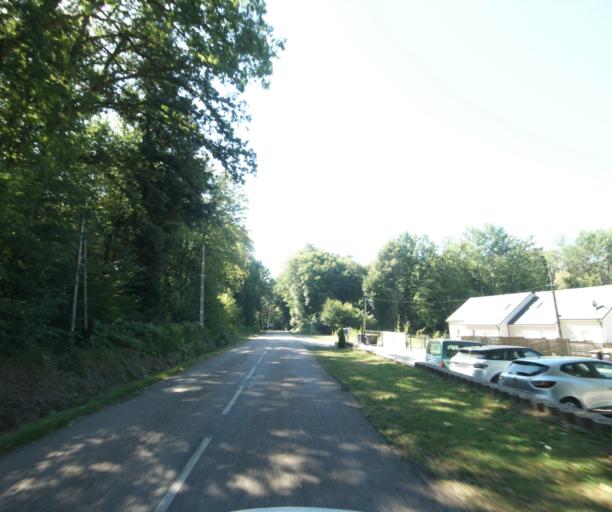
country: FR
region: Lorraine
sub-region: Departement des Vosges
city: Epinal
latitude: 48.1488
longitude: 6.4675
